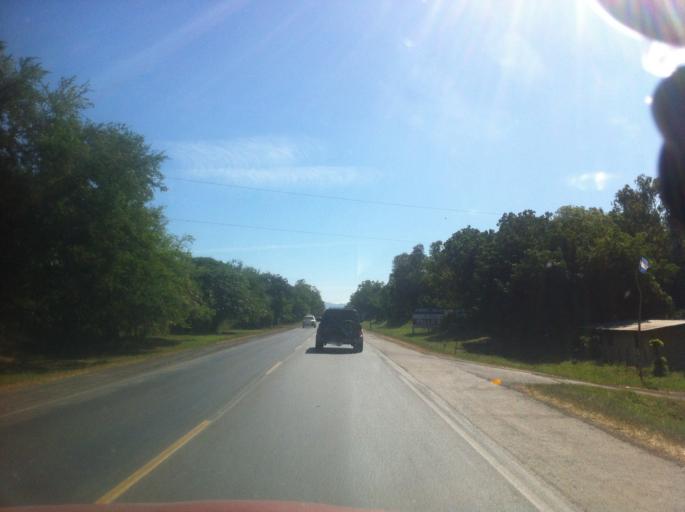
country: NI
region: Managua
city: Tipitapa
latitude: 12.2147
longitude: -86.0987
